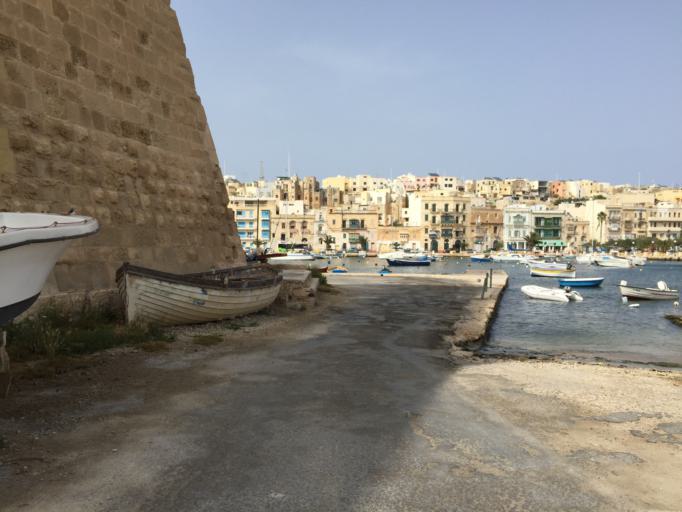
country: MT
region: Bormla
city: Cospicua
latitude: 35.8879
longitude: 14.5255
